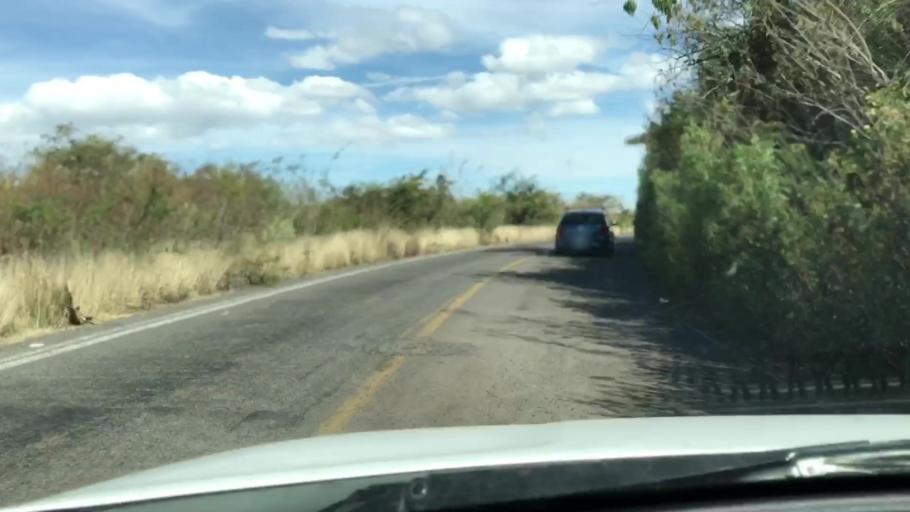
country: MX
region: Jalisco
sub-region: Zacoalco de Torres
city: Barranca de Otates (Barranca de Otatan)
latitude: 20.2284
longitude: -103.6883
